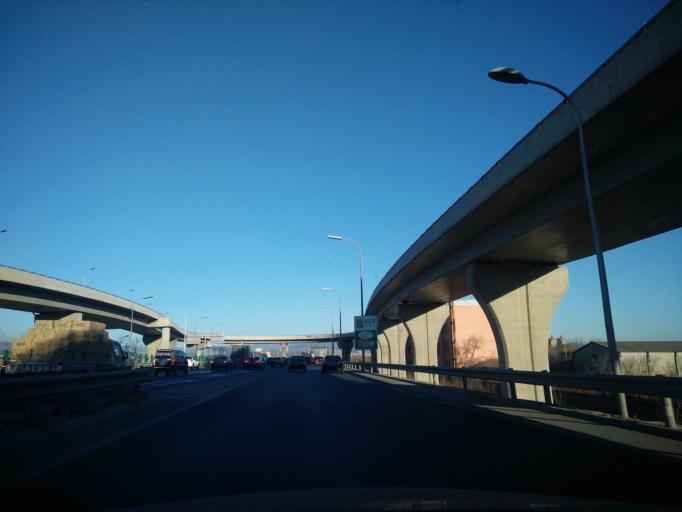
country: CN
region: Beijing
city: Lugu
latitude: 39.8665
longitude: 116.2066
